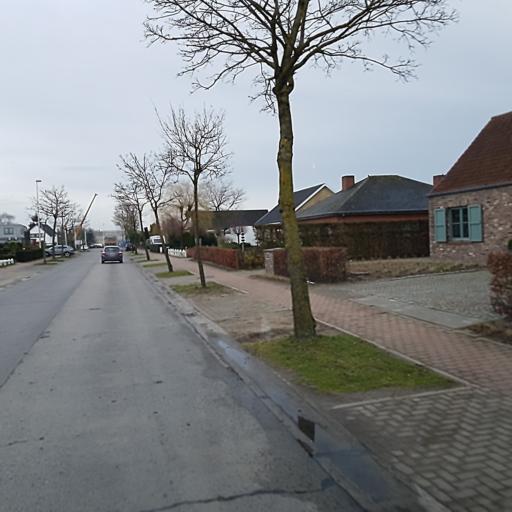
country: BE
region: Flanders
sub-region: Provincie Oost-Vlaanderen
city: Maldegem
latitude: 51.2030
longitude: 3.4665
